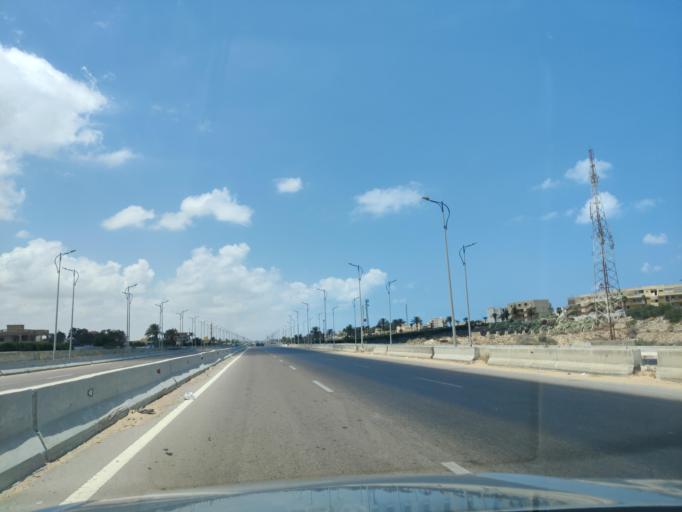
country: EG
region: Muhafazat Matruh
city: Al `Alamayn
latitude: 30.9313
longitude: 29.4792
